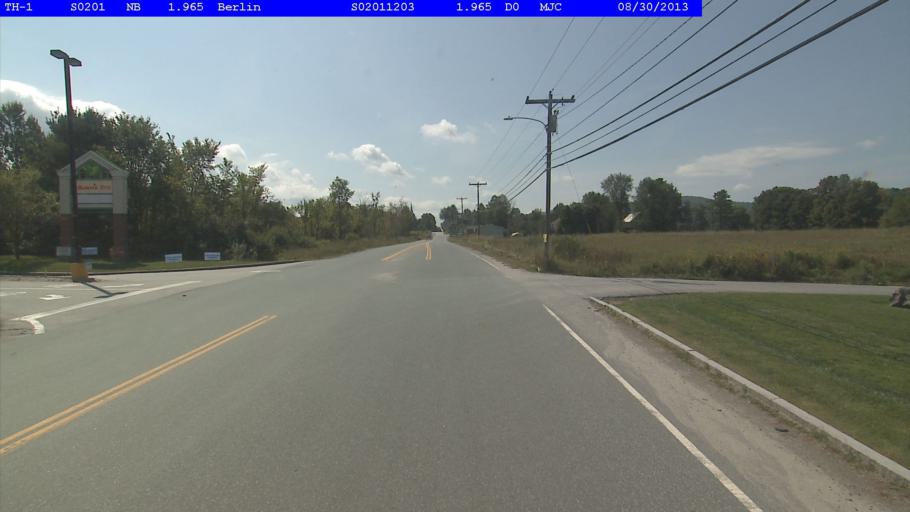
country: US
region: Vermont
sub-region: Washington County
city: Montpelier
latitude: 44.2123
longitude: -72.5752
